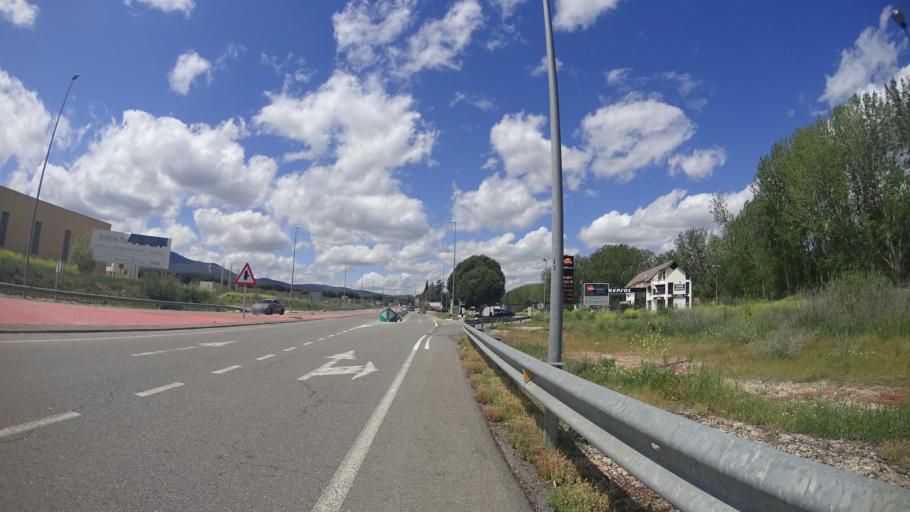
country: ES
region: Madrid
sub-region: Provincia de Madrid
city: Pelayos de la Presa
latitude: 40.3653
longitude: -4.3139
